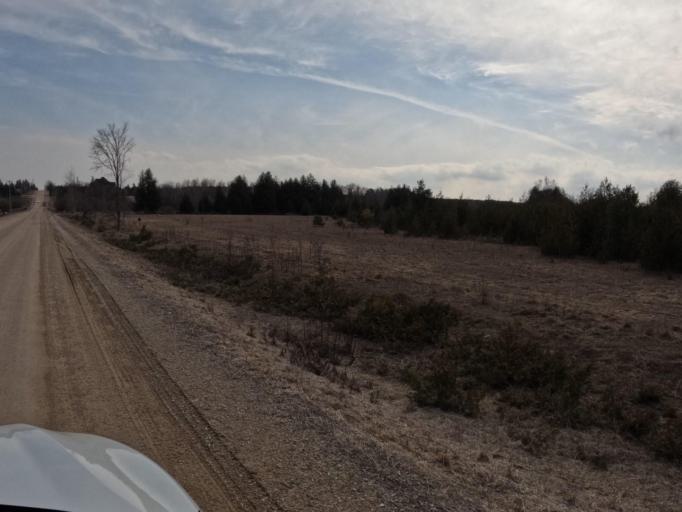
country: CA
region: Ontario
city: Orangeville
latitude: 43.8925
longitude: -80.2996
